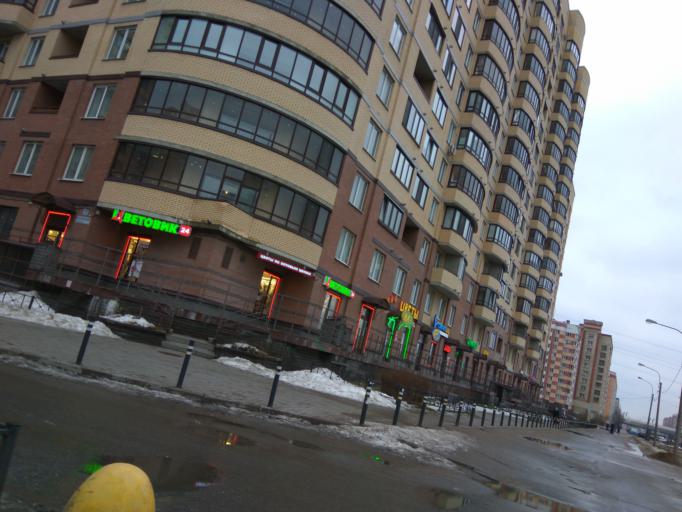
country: RU
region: Leningrad
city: Untolovo
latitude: 60.0060
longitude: 30.2223
